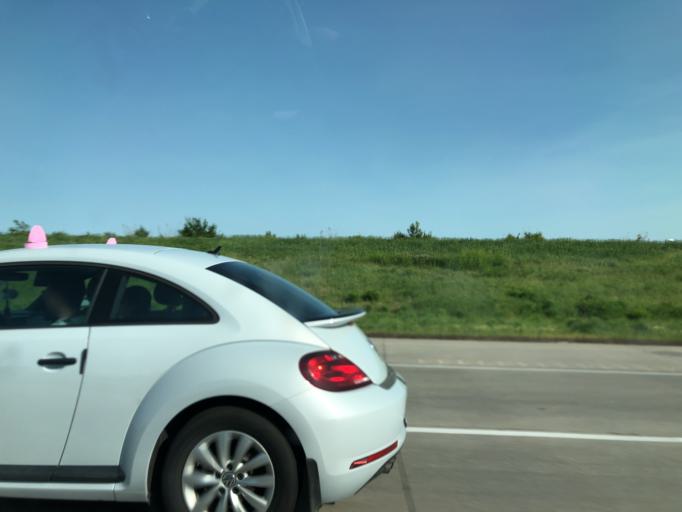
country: US
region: Nebraska
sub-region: Lancaster County
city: Waverly
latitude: 40.9301
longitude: -96.4445
